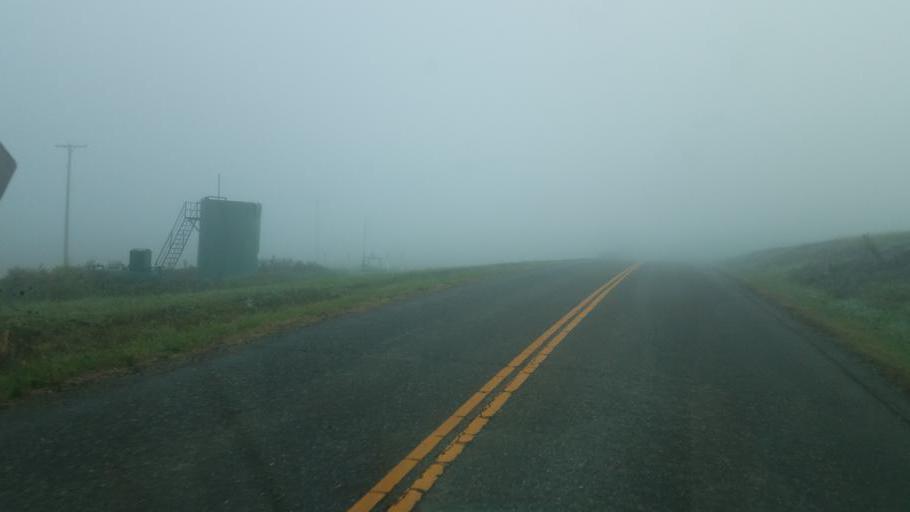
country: US
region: Ohio
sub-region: Tuscarawas County
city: Sugarcreek
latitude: 40.5016
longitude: -81.6111
